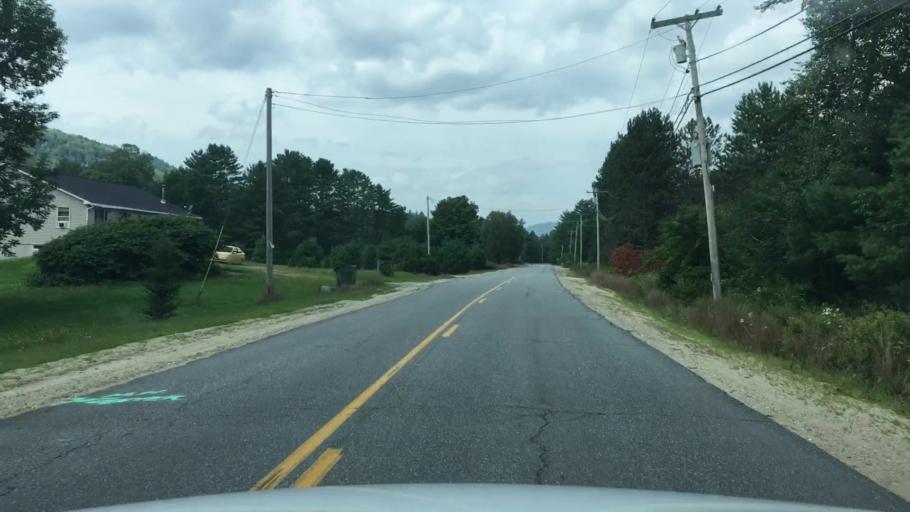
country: US
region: Maine
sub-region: Oxford County
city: Rumford
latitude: 44.5140
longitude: -70.6206
